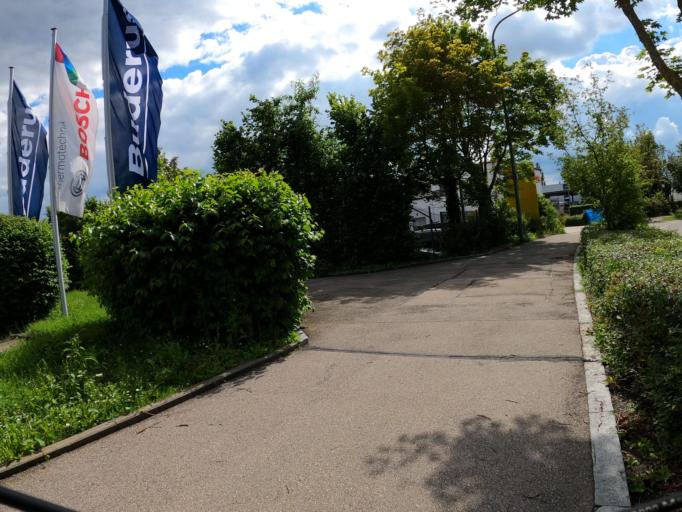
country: DE
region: Bavaria
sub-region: Swabia
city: Neu-Ulm
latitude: 48.3882
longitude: 10.0407
